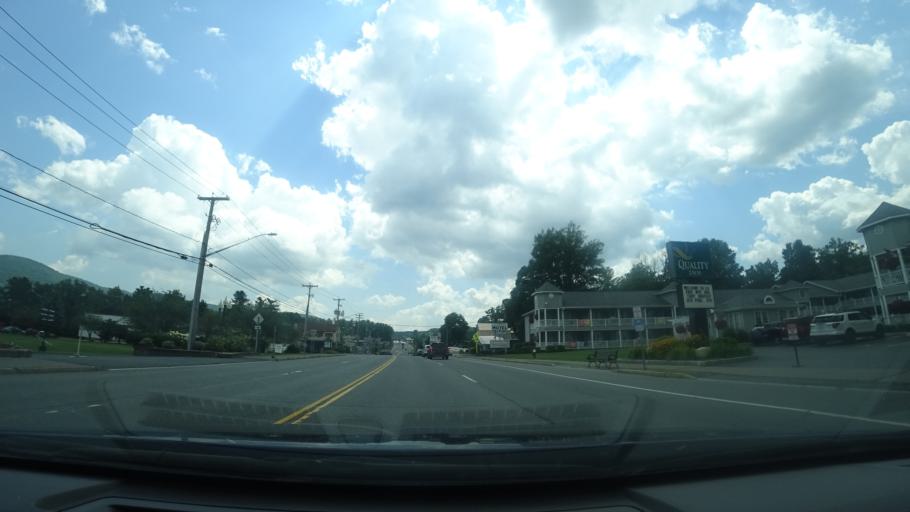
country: US
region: New York
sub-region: Warren County
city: Glens Falls North
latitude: 43.4202
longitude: -73.7141
